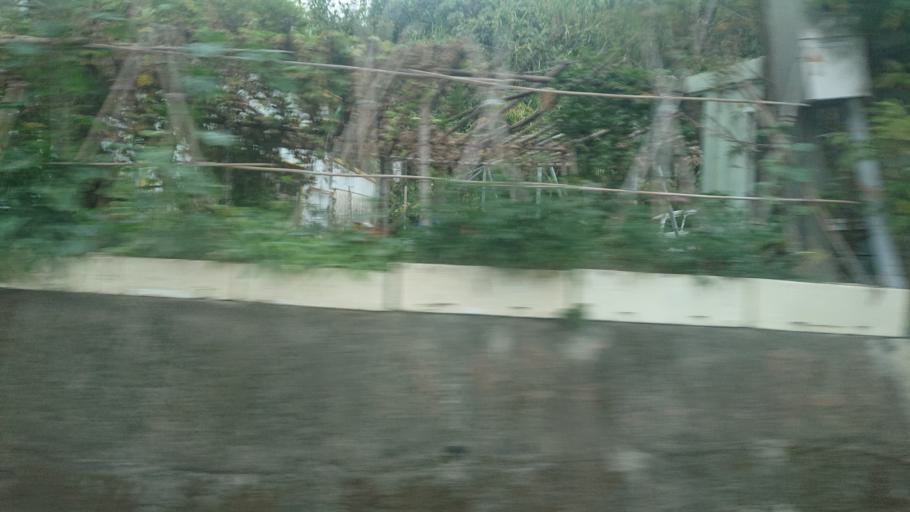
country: TW
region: Taiwan
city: Lugu
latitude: 23.6036
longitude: 120.7081
